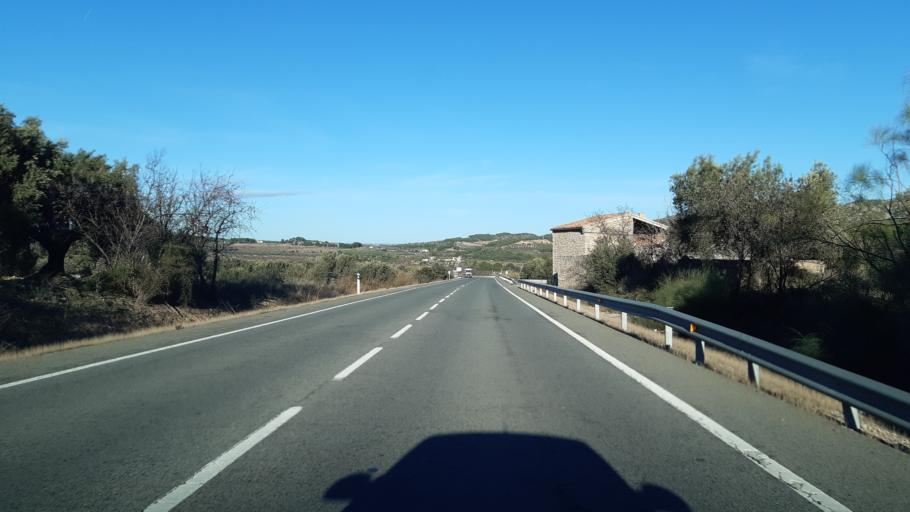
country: ES
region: Catalonia
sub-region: Provincia de Tarragona
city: la Fatarella
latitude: 41.1026
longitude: 0.5242
